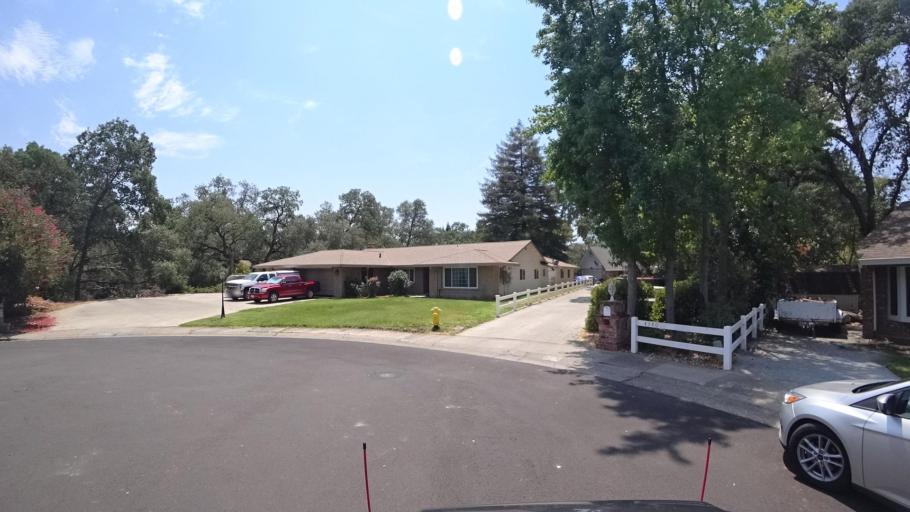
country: US
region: California
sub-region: Placer County
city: Rocklin
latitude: 38.7997
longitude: -121.2369
